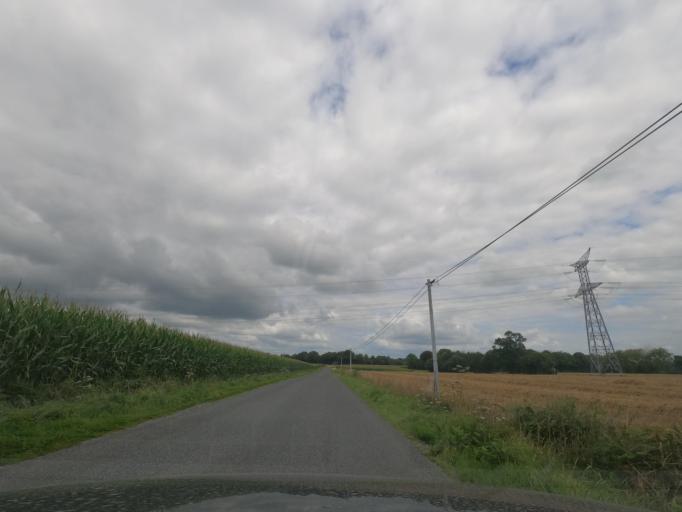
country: FR
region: Pays de la Loire
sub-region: Departement de la Mayenne
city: Fougerolles-du-Plessis
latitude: 48.4967
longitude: -0.9262
